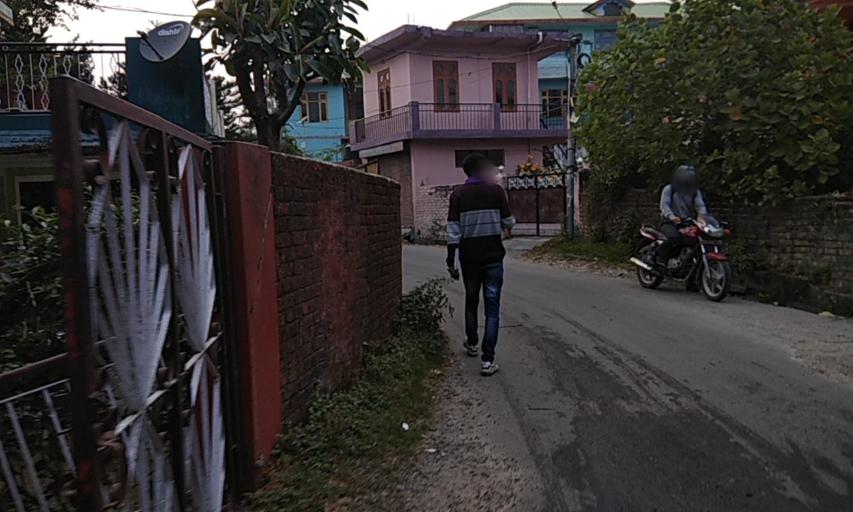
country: IN
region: Himachal Pradesh
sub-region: Kangra
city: Palampur
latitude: 32.1158
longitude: 76.5339
